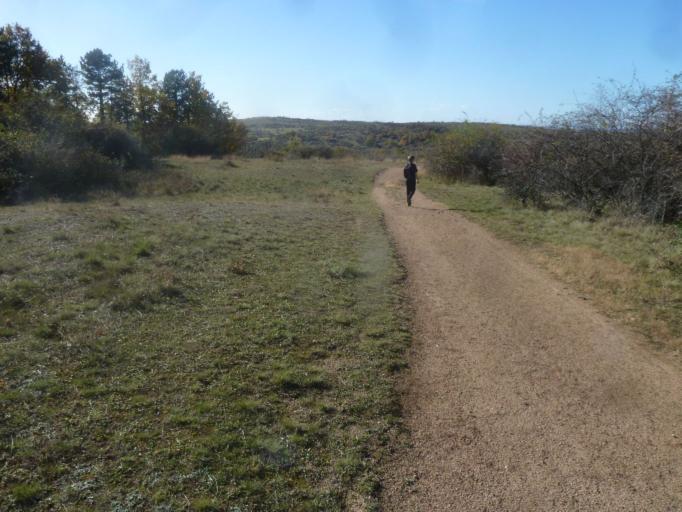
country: HU
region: Fejer
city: Pakozd
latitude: 47.2317
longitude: 18.5367
